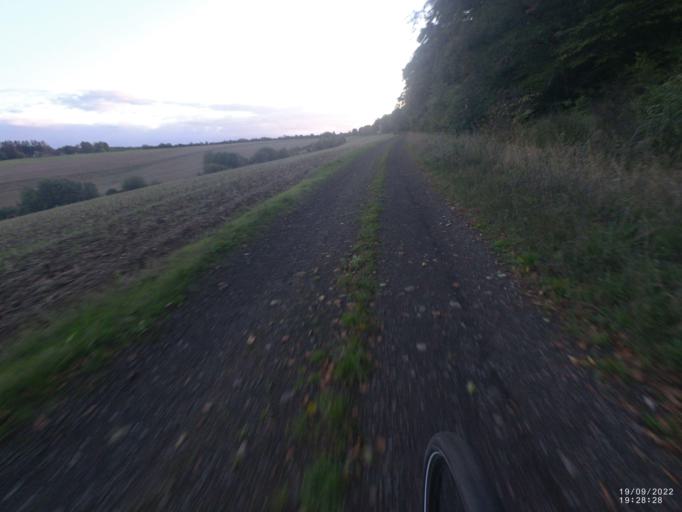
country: DE
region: Rheinland-Pfalz
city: Brockscheid
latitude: 50.1392
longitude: 6.8546
